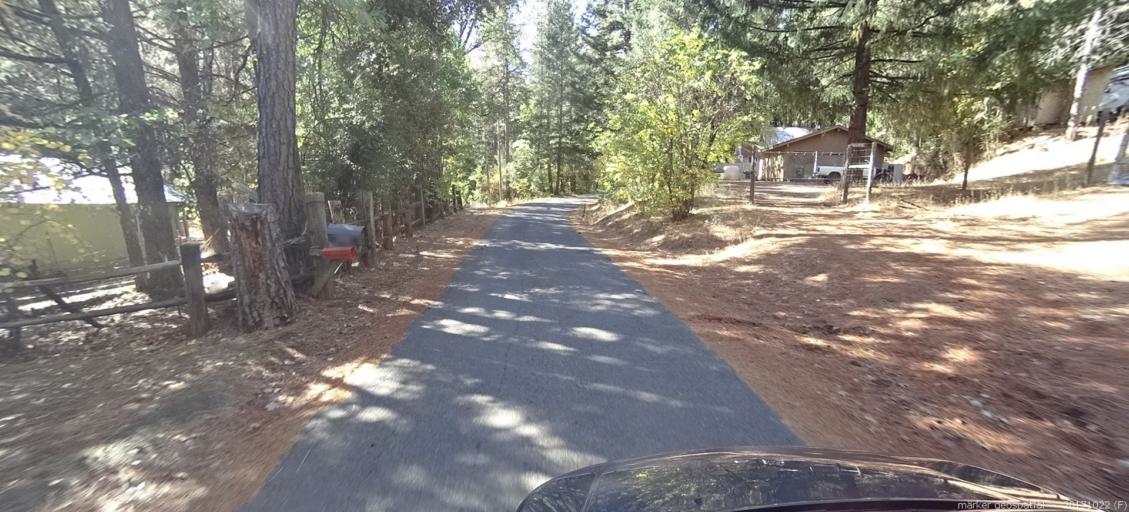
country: US
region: California
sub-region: Shasta County
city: Central Valley (historical)
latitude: 40.9383
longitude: -122.4504
